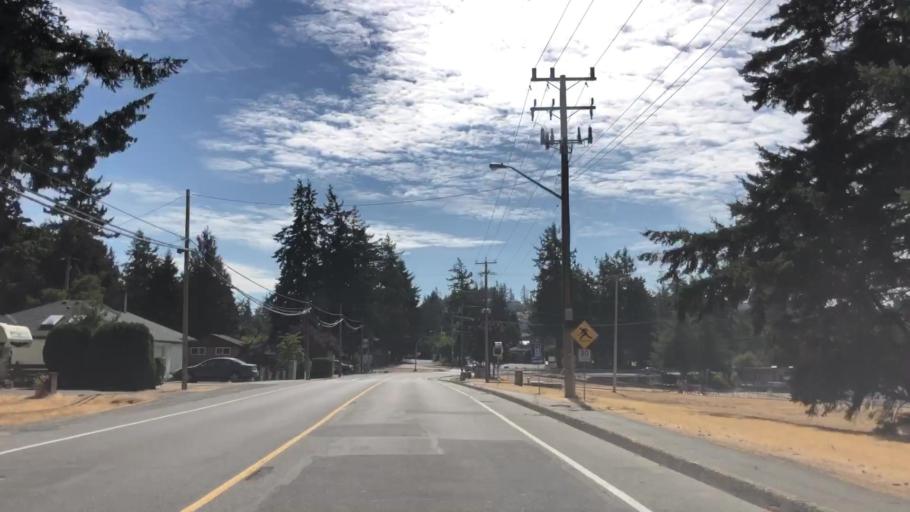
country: CA
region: British Columbia
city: Colwood
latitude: 48.4231
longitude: -123.4924
